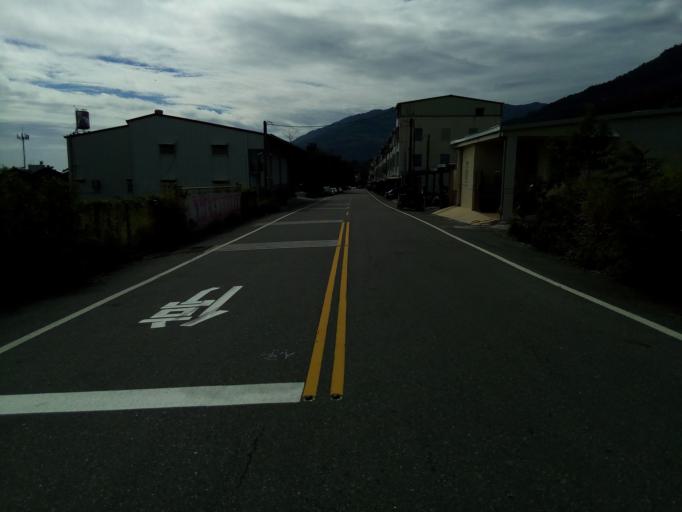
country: TW
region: Taiwan
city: Taitung City
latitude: 22.6174
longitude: 121.0067
